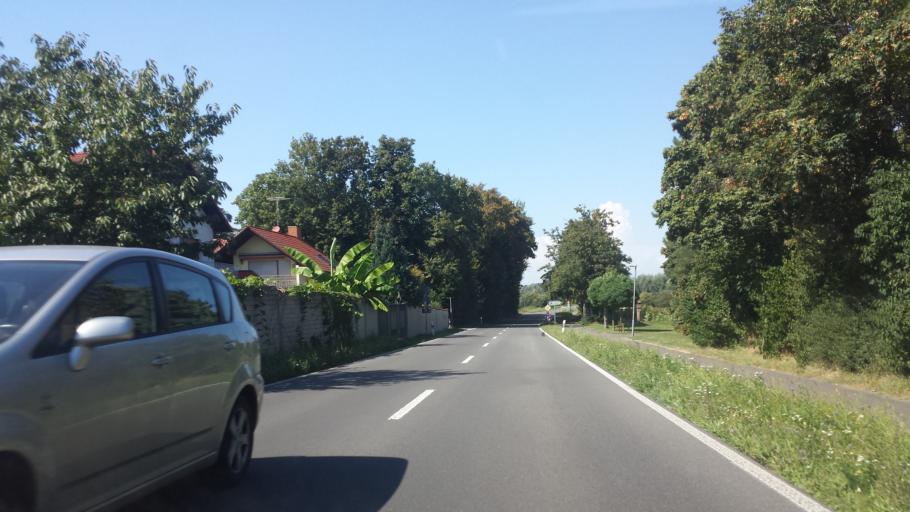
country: DE
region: Baden-Wuerttemberg
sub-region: Karlsruhe Region
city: Oberhausen-Rheinhausen
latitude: 49.2692
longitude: 8.4765
